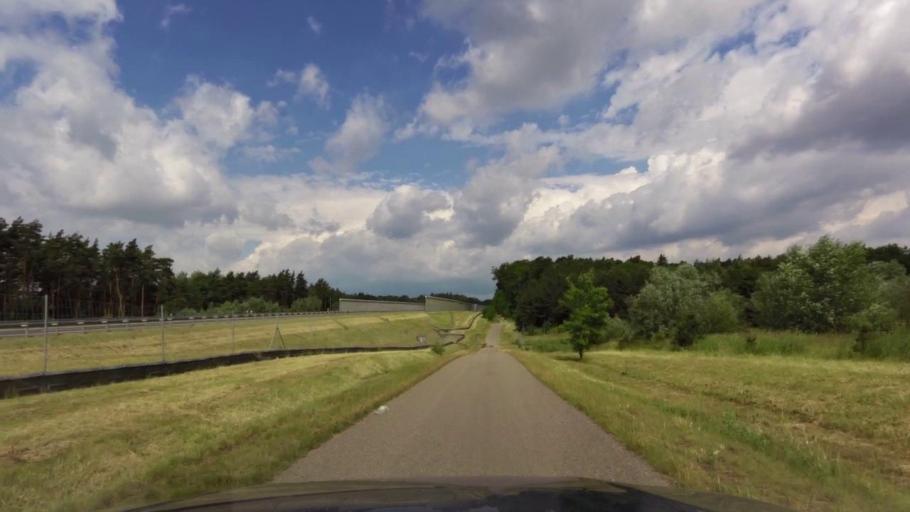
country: PL
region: West Pomeranian Voivodeship
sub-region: Powiat pyrzycki
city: Lipiany
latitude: 52.9621
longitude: 14.9244
